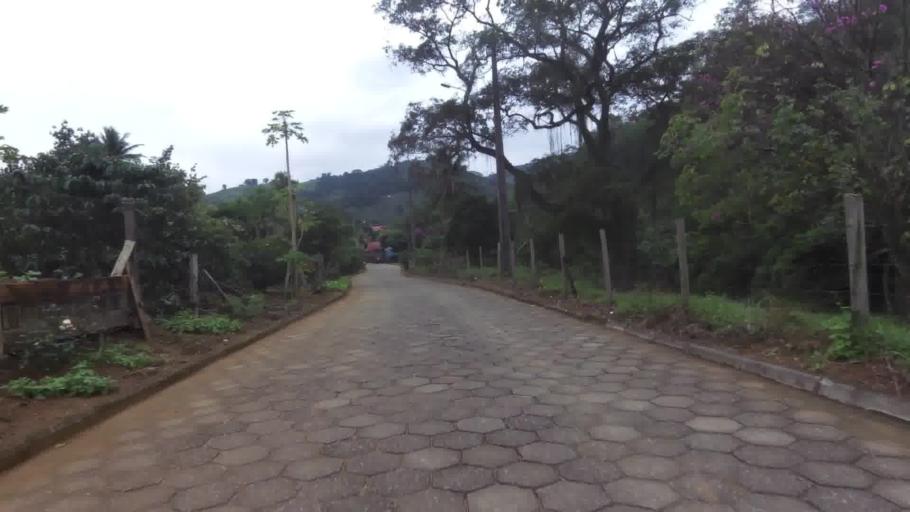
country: BR
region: Espirito Santo
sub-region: Iconha
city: Iconha
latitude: -20.7771
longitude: -40.8282
